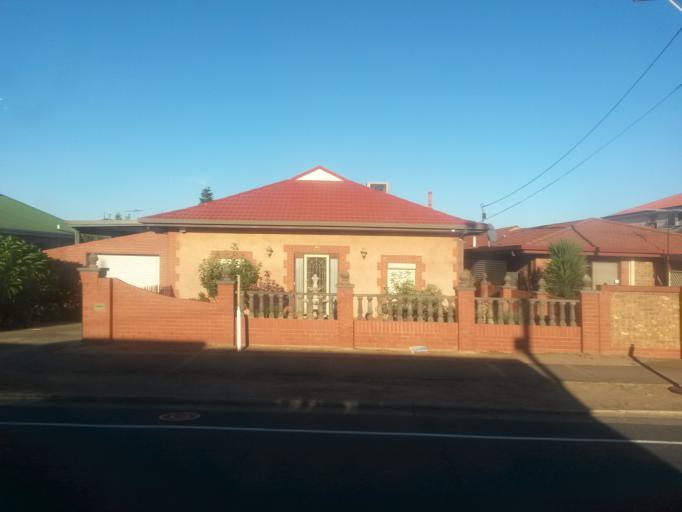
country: AU
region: South Australia
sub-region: Port Adelaide Enfield
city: Alberton
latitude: -34.8549
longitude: 138.5291
